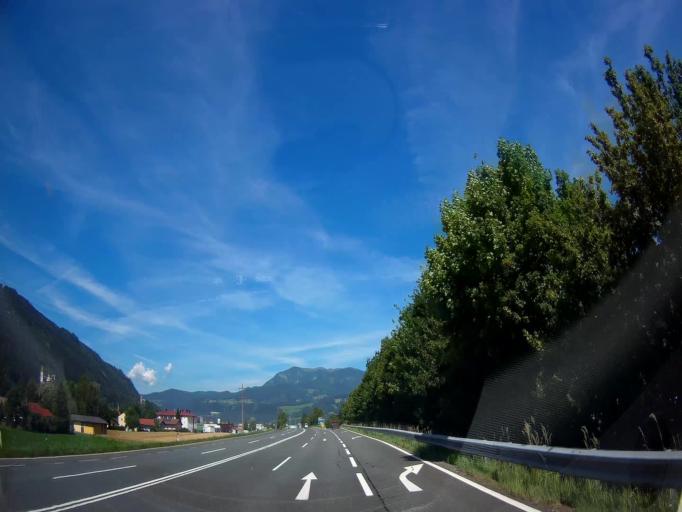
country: AT
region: Carinthia
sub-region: Politischer Bezirk Sankt Veit an der Glan
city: Friesach
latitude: 46.9502
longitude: 14.4193
